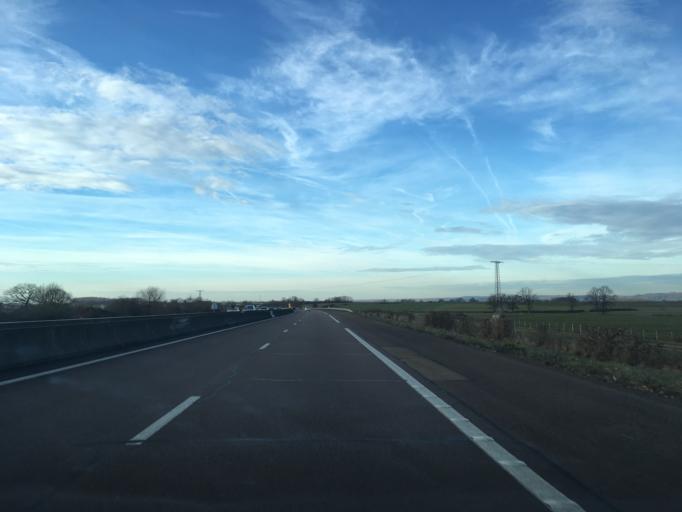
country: FR
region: Bourgogne
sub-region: Departement de la Cote-d'Or
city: Semur-en-Auxois
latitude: 47.4633
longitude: 4.2499
